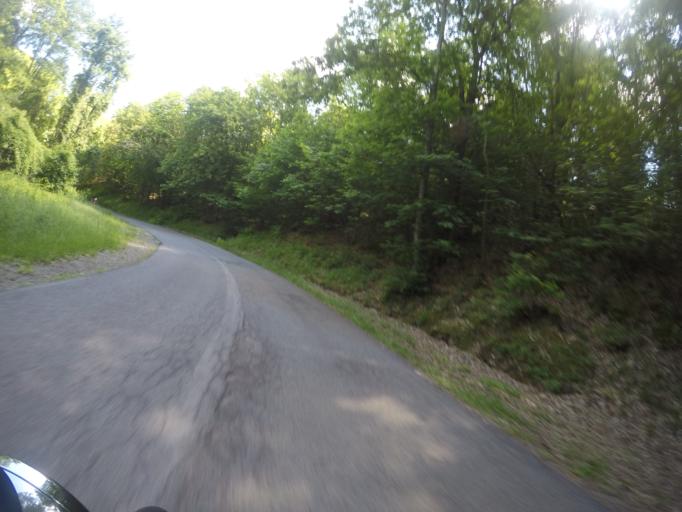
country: IT
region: Tuscany
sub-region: Provincia di Lucca
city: Careggine
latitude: 44.1342
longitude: 10.3466
